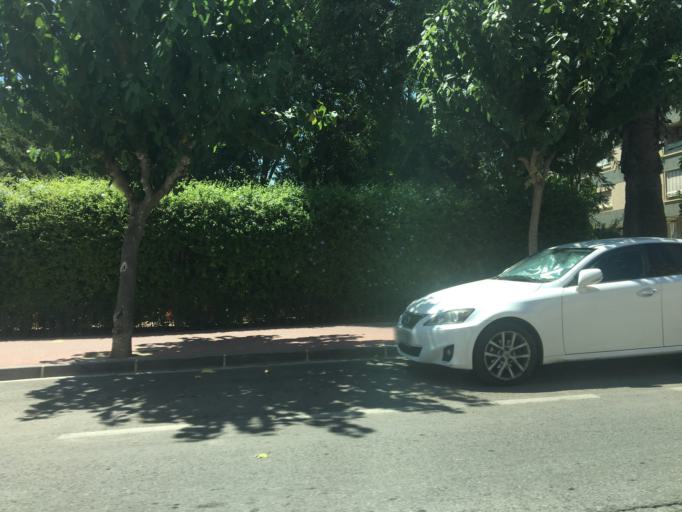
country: ES
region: Murcia
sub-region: Murcia
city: Murcia
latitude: 38.0039
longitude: -1.1149
